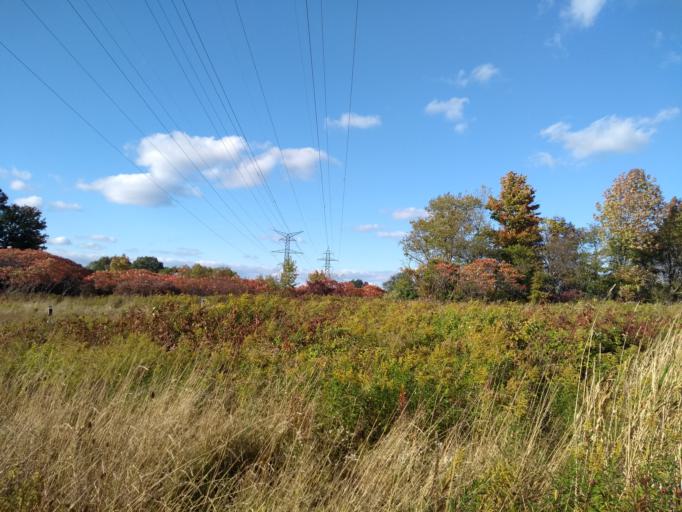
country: CA
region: Ontario
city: Thorold
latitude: 43.0961
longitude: -79.2742
